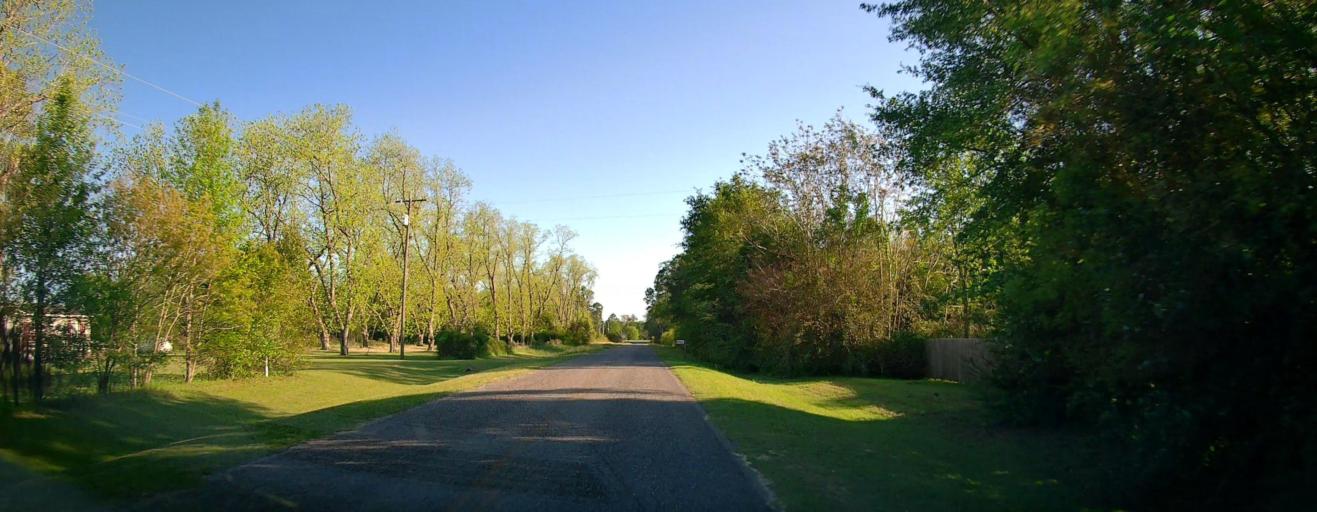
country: US
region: Georgia
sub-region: Ben Hill County
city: Fitzgerald
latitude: 31.6939
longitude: -83.1536
